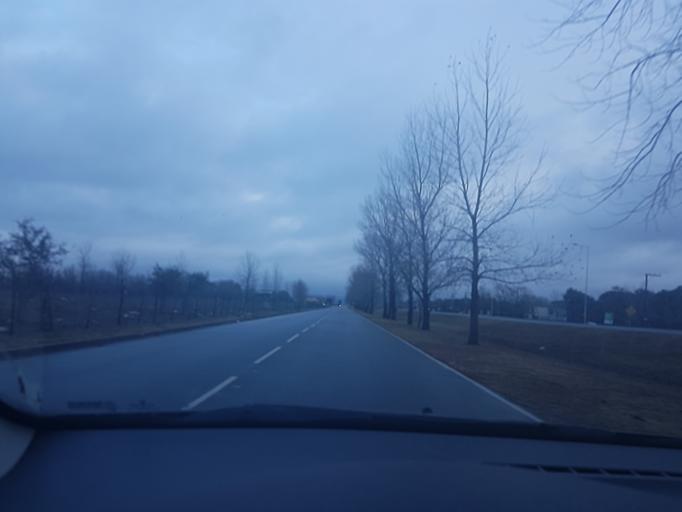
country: AR
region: Cordoba
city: Villa Allende
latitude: -31.3039
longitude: -64.2306
